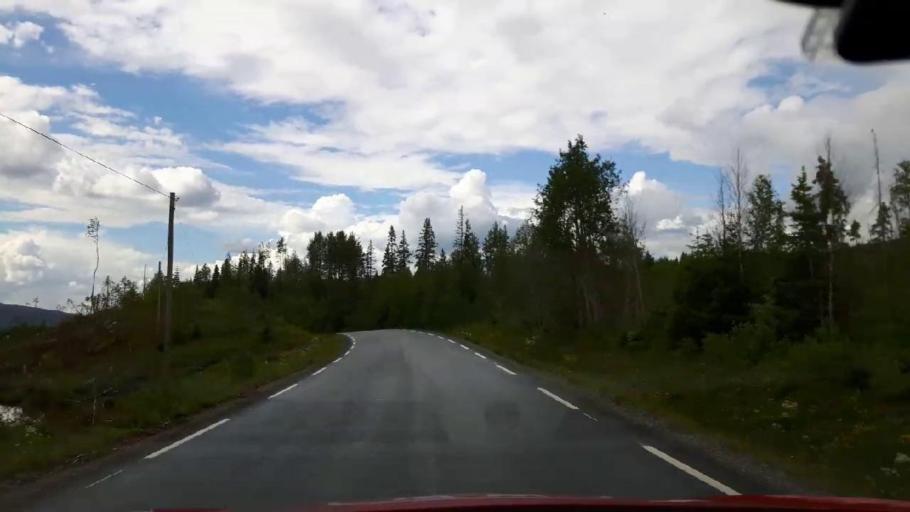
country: NO
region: Nord-Trondelag
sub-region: Lierne
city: Sandvika
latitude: 64.0988
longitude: 14.0315
